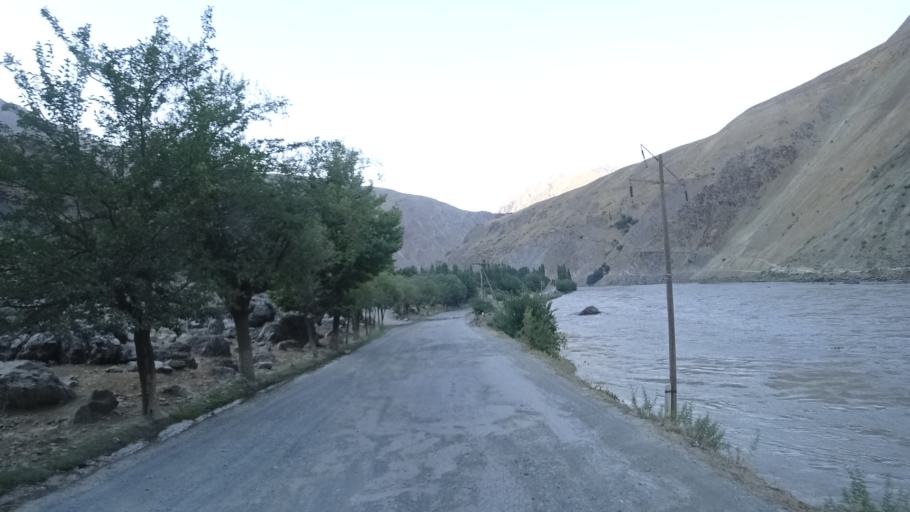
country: TJ
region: Gorno-Badakhshan
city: Qalaikhumb
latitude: 38.4413
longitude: 70.7612
